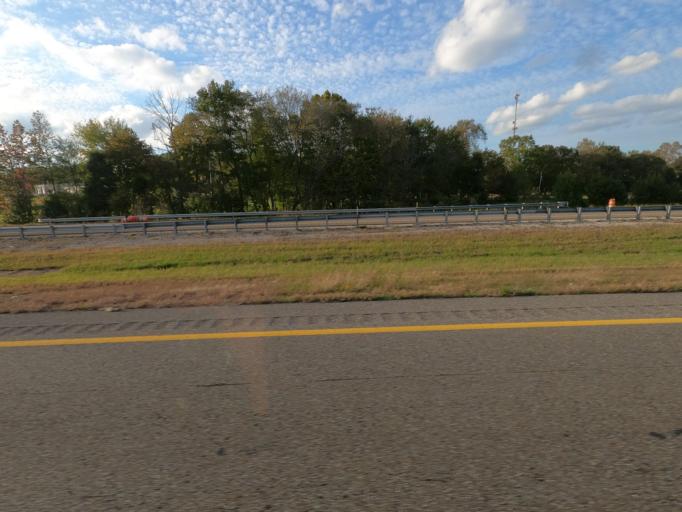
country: US
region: Tennessee
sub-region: Humphreys County
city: New Johnsonville
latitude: 35.8483
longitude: -88.0713
